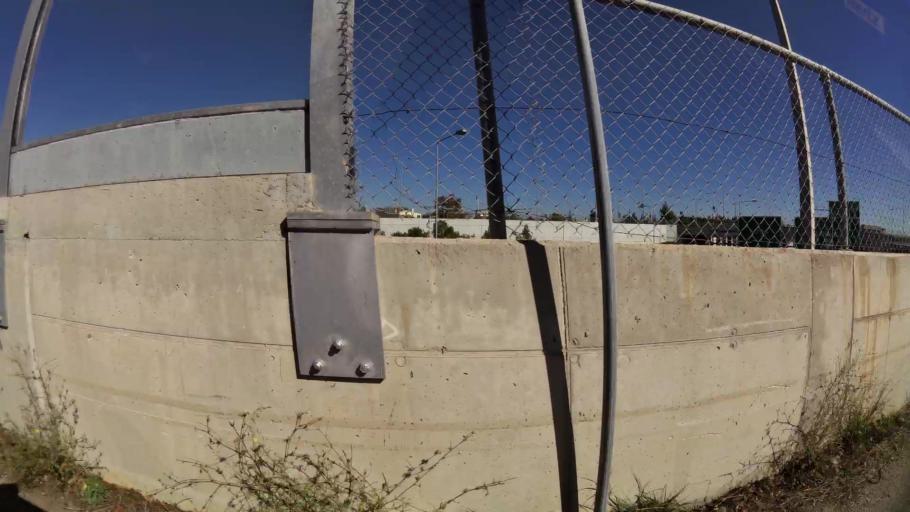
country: GR
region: Attica
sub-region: Nomarchia Anatolikis Attikis
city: Pallini
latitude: 37.9956
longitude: 23.8688
